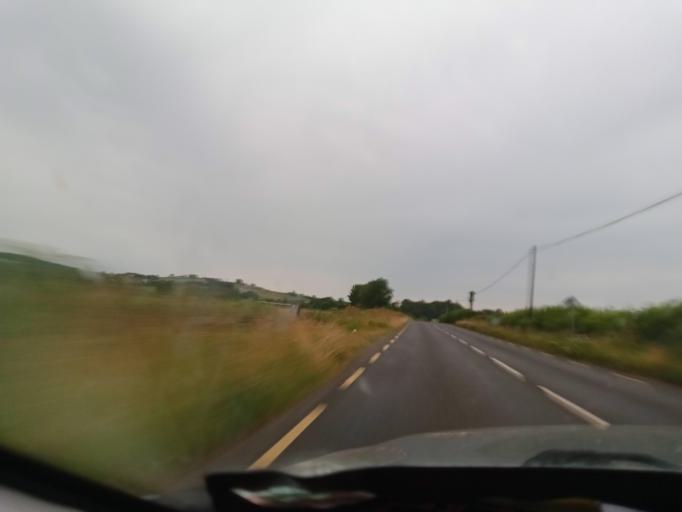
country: IE
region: Leinster
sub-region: Laois
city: Mountmellick
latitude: 53.1295
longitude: -7.3892
